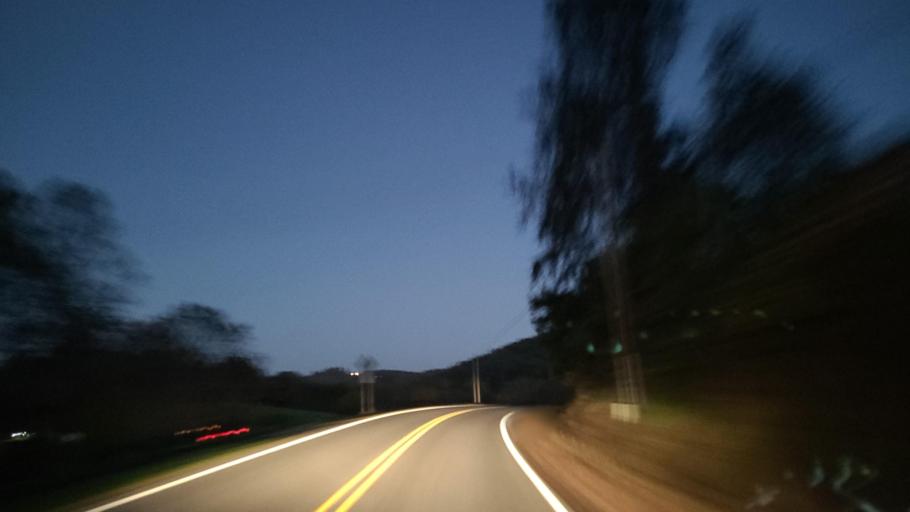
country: US
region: North Carolina
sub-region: Clay County
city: Hayesville
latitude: 34.9756
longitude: -83.8708
